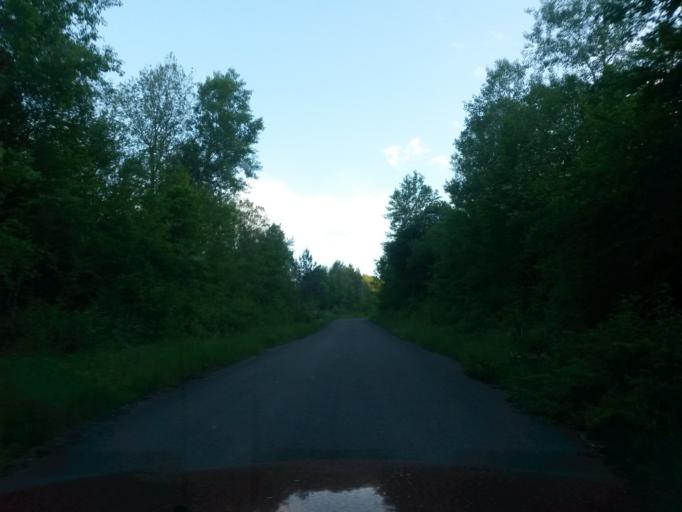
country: UA
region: Zakarpattia
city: Velykyi Bereznyi
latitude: 48.8299
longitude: 22.3643
